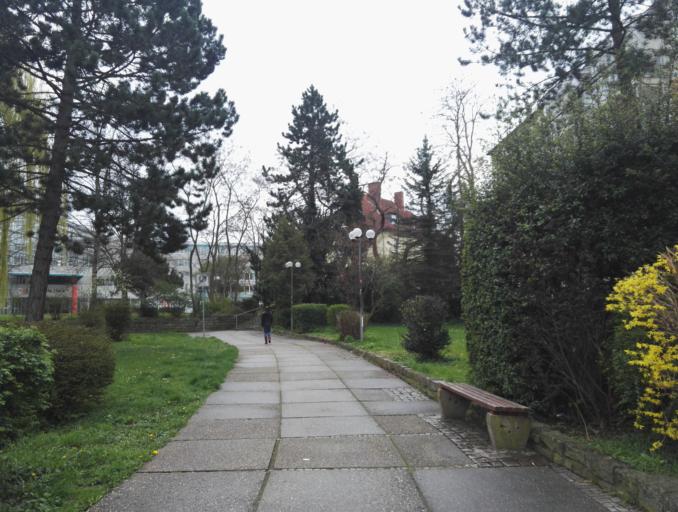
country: DE
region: Saxony-Anhalt
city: Halberstadt
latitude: 51.8961
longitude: 11.0584
